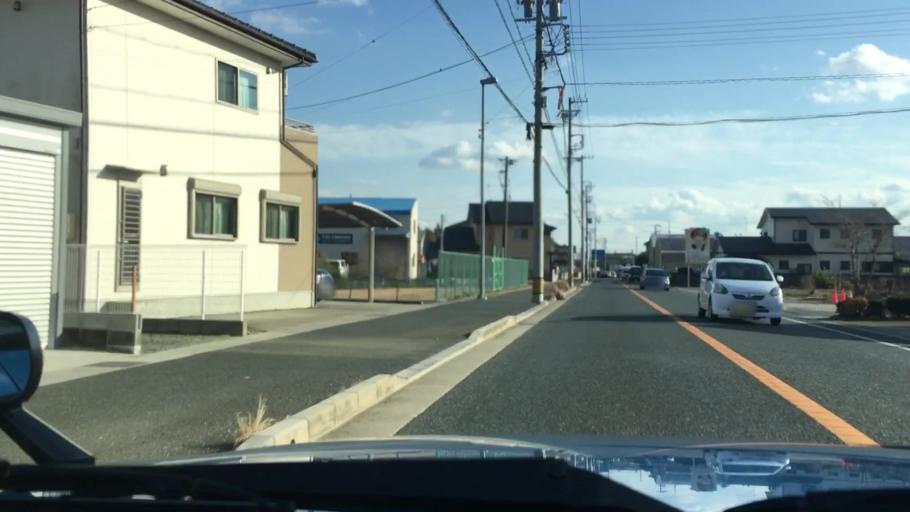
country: JP
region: Shizuoka
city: Hamamatsu
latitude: 34.7541
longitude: 137.6710
